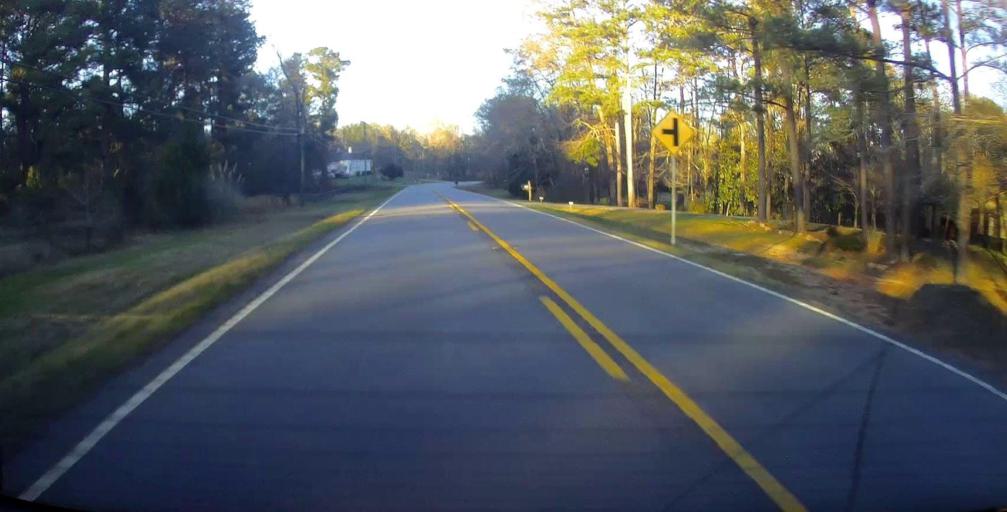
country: US
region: Alabama
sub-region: Lee County
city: Smiths Station
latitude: 32.6516
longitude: -85.0114
